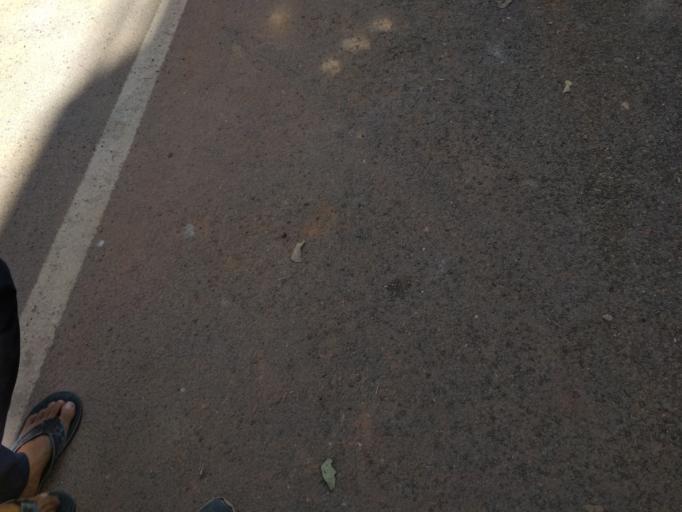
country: IN
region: Karnataka
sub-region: Bangalore Urban
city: Yelahanka
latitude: 13.0701
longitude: 77.5745
